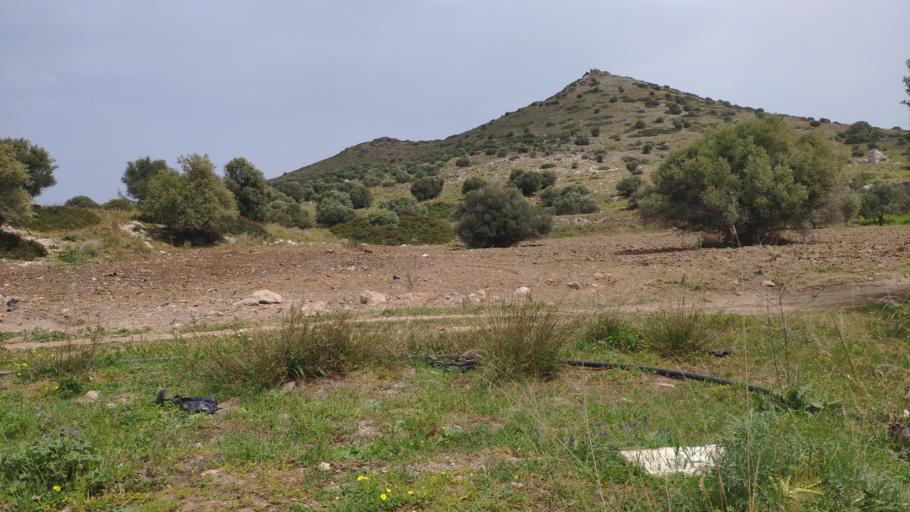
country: GR
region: Attica
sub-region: Nomarchia Anatolikis Attikis
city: Lavrio
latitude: 37.7378
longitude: 24.0493
